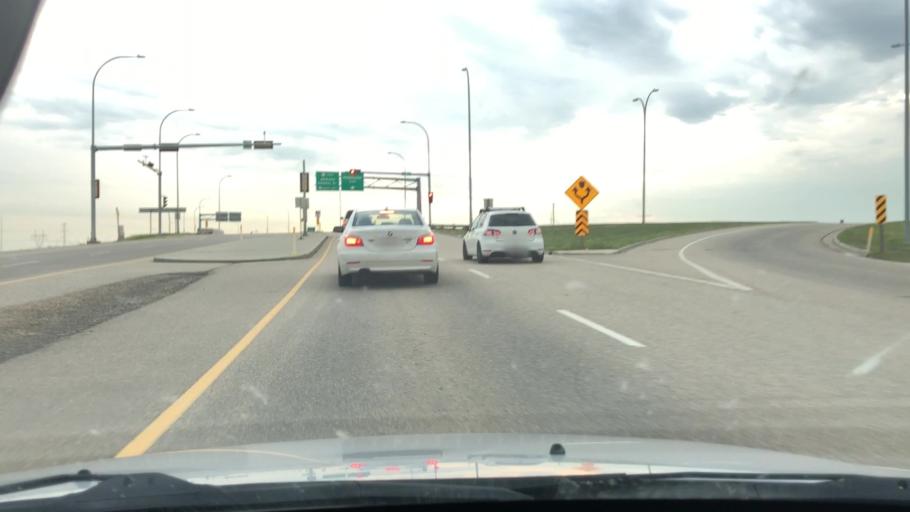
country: CA
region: Alberta
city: Devon
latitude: 53.4676
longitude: -113.6288
